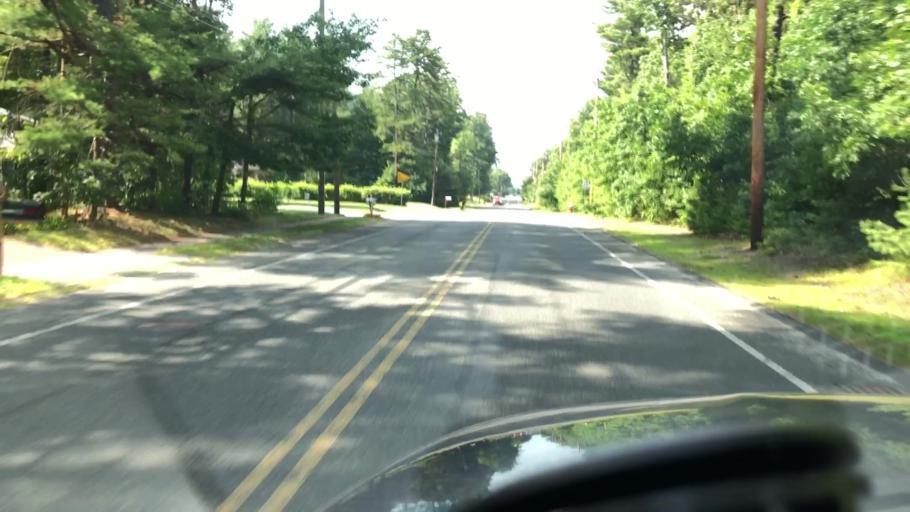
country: US
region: Massachusetts
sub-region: Hampshire County
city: Southampton
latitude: 42.1984
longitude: -72.6879
